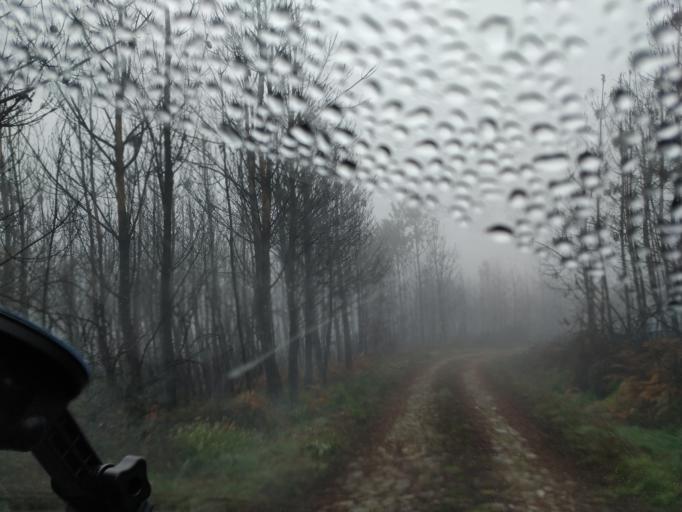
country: PT
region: Vila Real
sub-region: Vila Real
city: Vila Real
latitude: 41.3522
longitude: -7.7313
